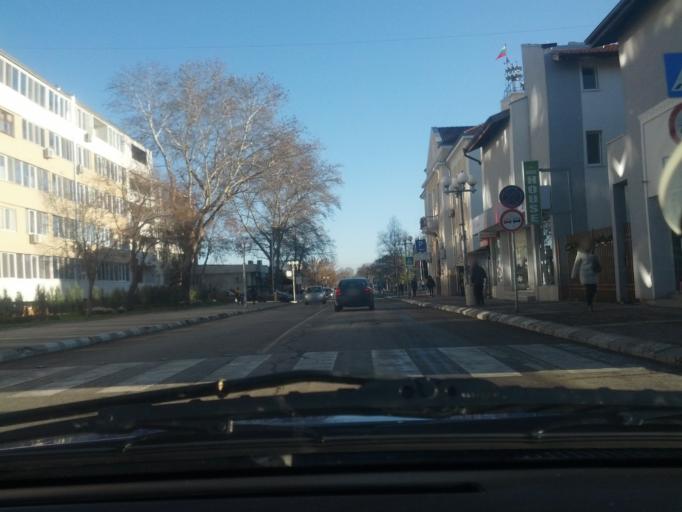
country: BG
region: Vratsa
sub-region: Obshtina Kozloduy
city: Kozloduy
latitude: 43.7786
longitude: 23.7270
